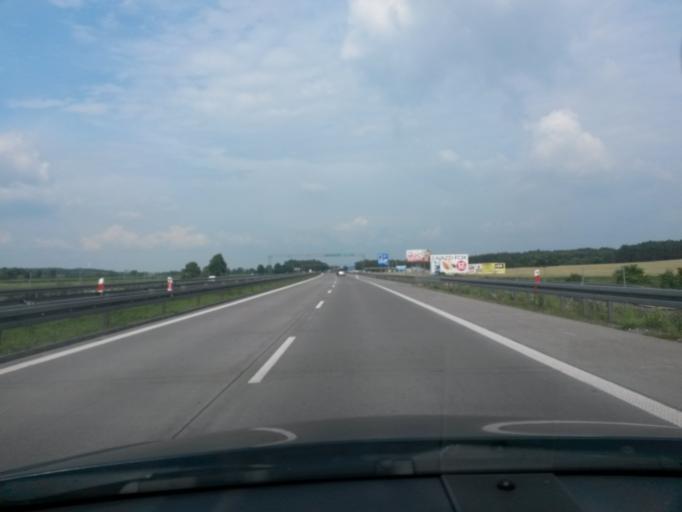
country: PL
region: Lodz Voivodeship
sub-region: Powiat piotrkowski
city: Wolborz
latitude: 51.5002
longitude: 19.8619
